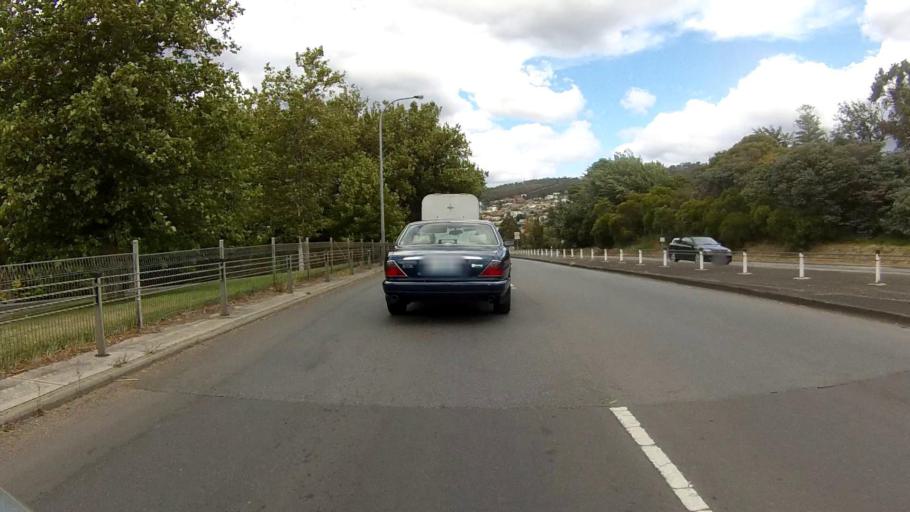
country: AU
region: Tasmania
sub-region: Hobart
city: Sandy Bay
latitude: -42.8931
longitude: 147.3184
